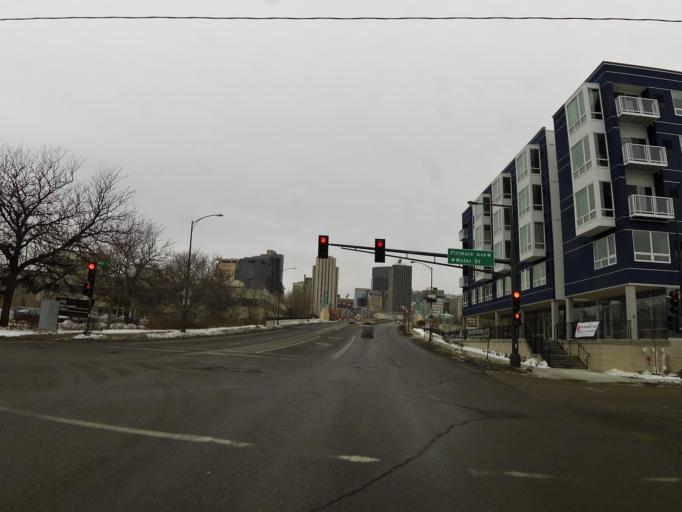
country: US
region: Minnesota
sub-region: Ramsey County
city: Saint Paul
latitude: 44.9393
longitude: -93.0893
